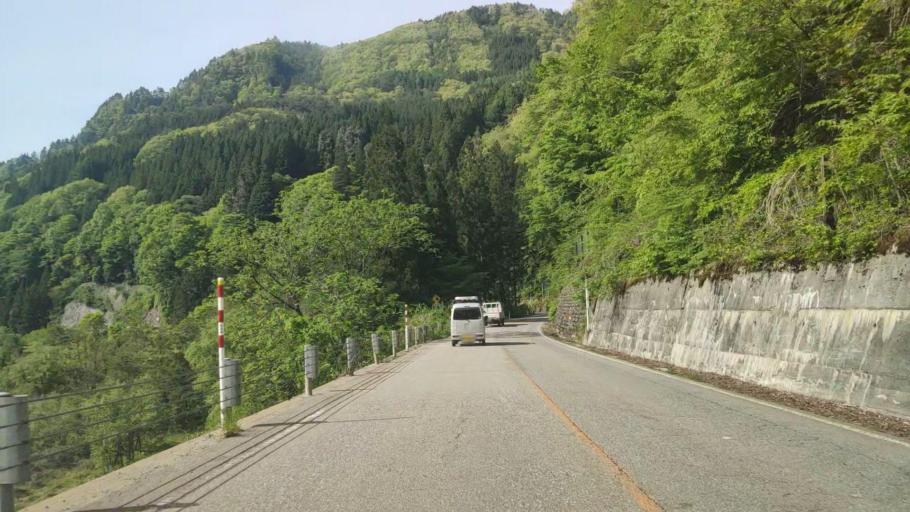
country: JP
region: Gifu
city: Takayama
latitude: 36.2716
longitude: 137.3926
